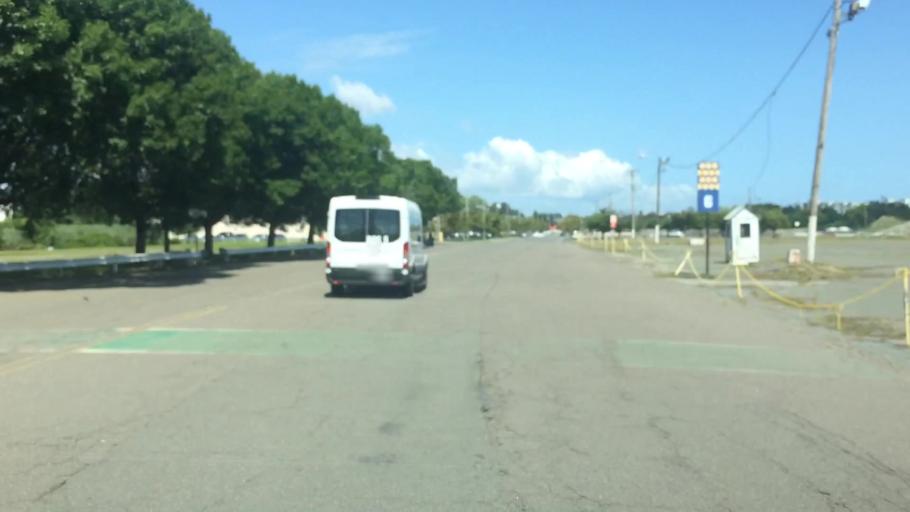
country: US
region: Massachusetts
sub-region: Suffolk County
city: Revere
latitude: 42.3957
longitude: -71.0016
